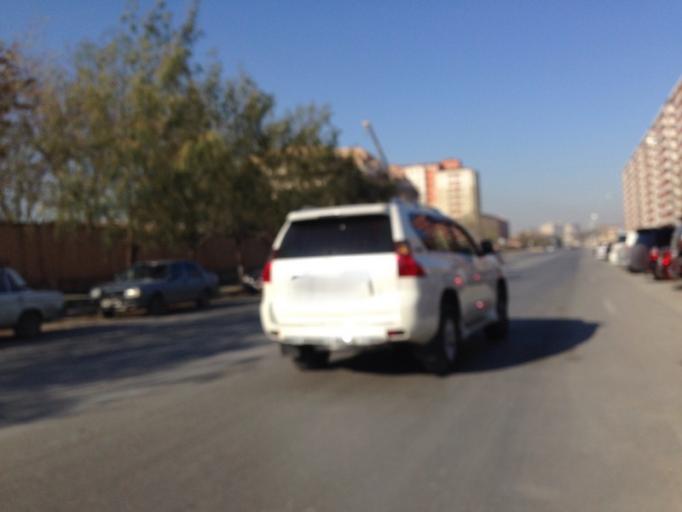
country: AZ
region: Baki
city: Baku
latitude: 40.4124
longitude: 49.8713
